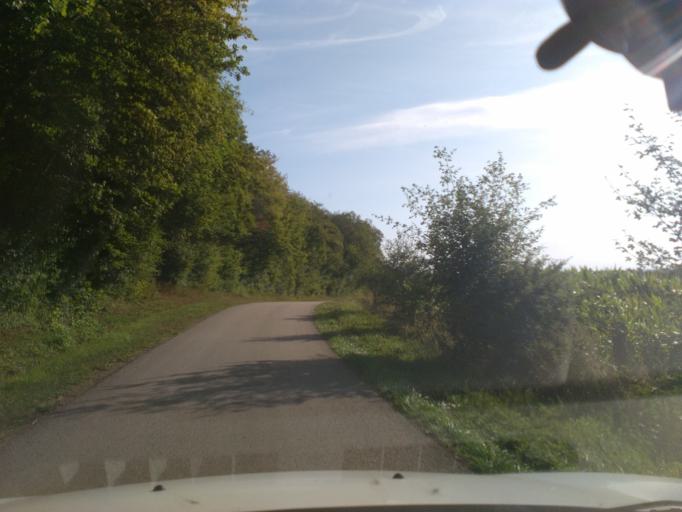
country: FR
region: Lorraine
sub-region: Departement des Vosges
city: Mirecourt
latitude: 48.3027
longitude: 6.0308
